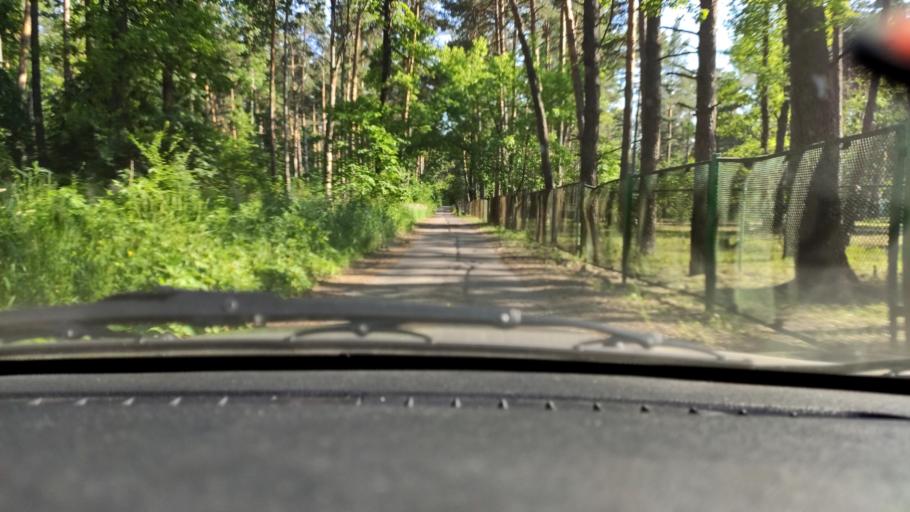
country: RU
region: Voronezj
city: Somovo
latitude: 51.7587
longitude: 39.3747
